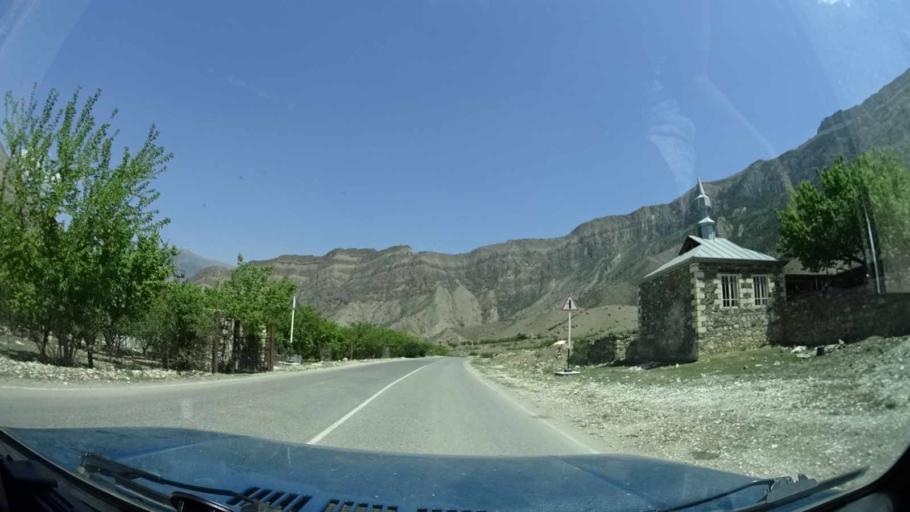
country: RU
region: Dagestan
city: Gergebil'
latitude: 42.4724
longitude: 47.0494
